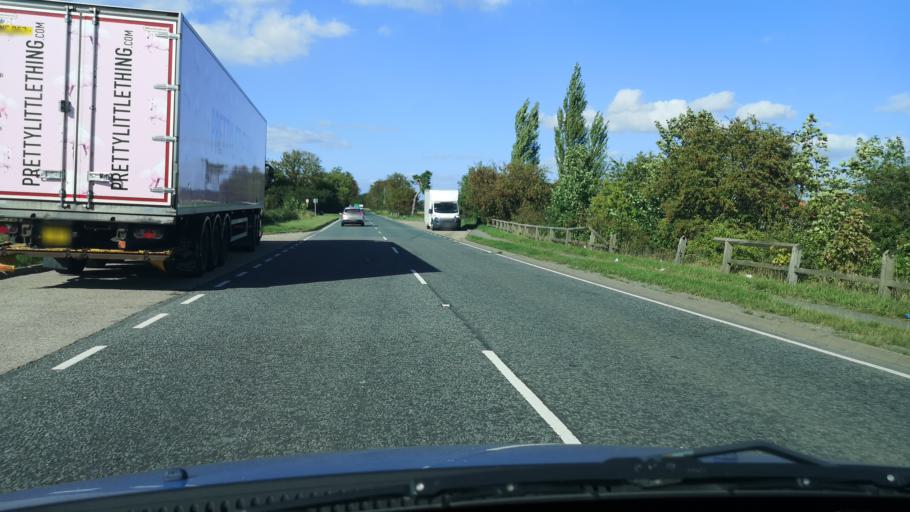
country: GB
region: England
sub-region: North Lincolnshire
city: Belton
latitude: 53.5722
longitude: -0.8177
